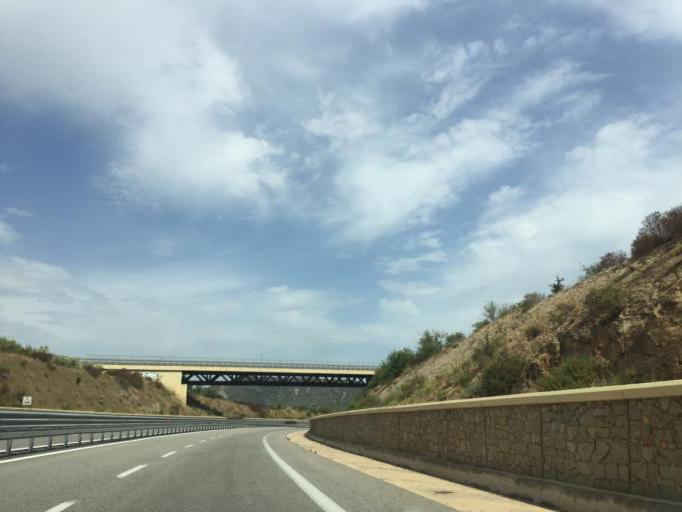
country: IT
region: Sardinia
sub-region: Provincia di Olbia-Tempio
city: San Teodoro
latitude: 40.7984
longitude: 9.5939
